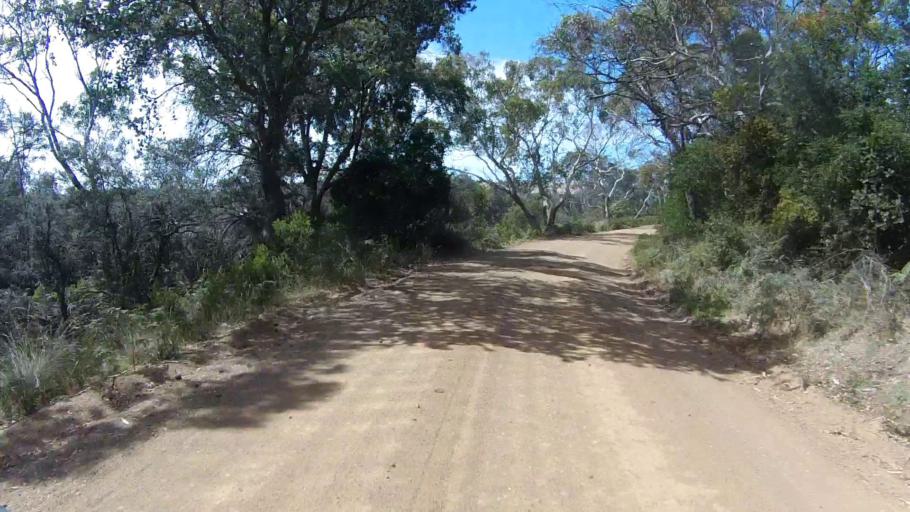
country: AU
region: Tasmania
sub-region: Clarence
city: Sandford
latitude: -43.0211
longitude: 147.4913
